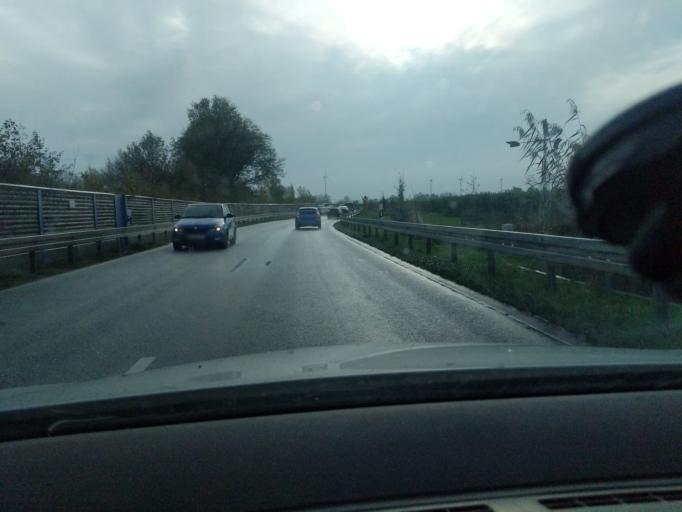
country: DE
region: Lower Saxony
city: Neu Wulmstorf
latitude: 53.5131
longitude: 9.8374
